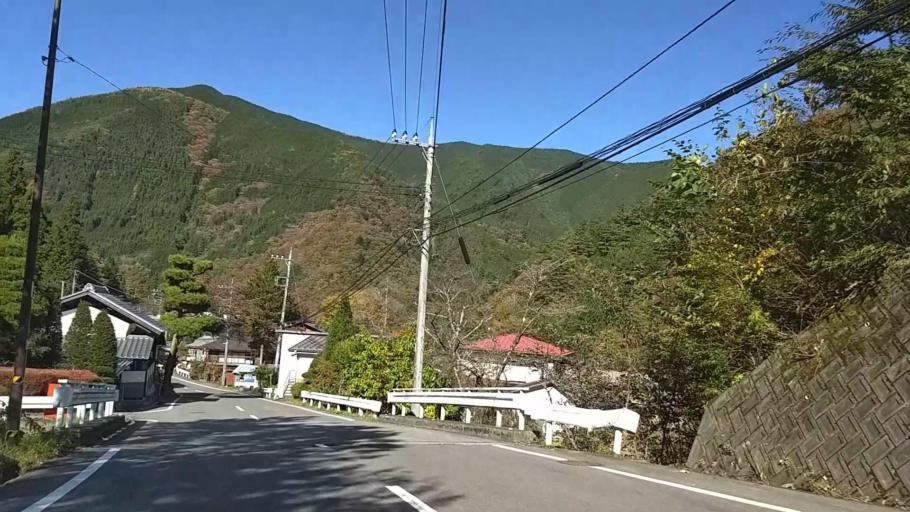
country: JP
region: Yamanashi
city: Otsuki
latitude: 35.7515
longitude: 138.9537
